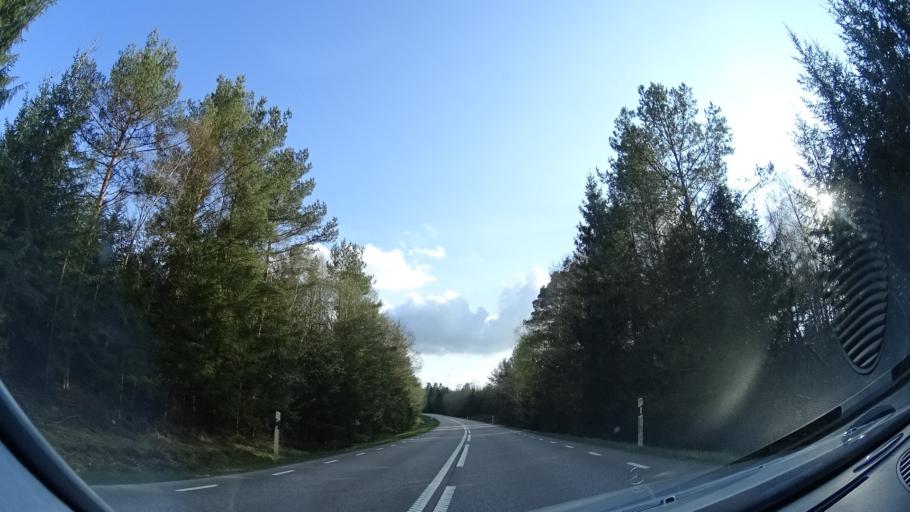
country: SE
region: Skane
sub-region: Klippans Kommun
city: Ljungbyhed
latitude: 56.1149
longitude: 13.2871
